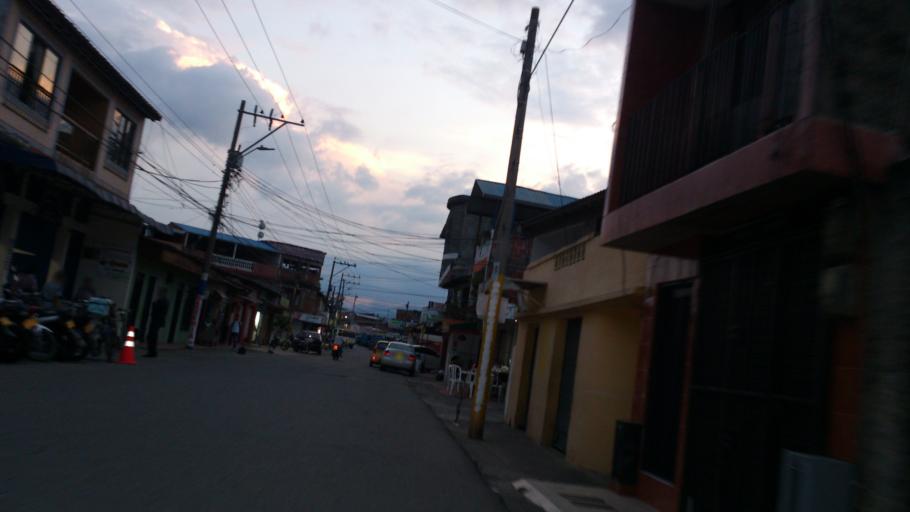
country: CO
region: Valle del Cauca
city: Jamundi
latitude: 3.2611
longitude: -76.5368
